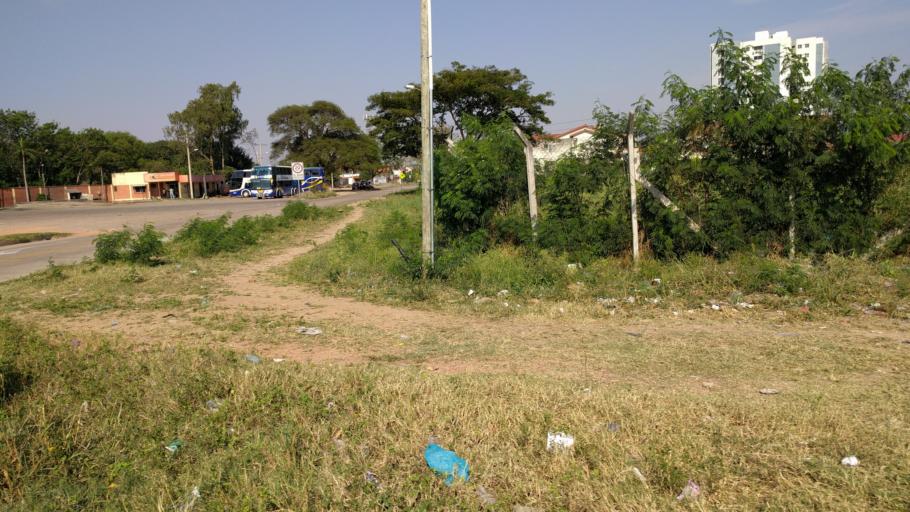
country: BO
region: Santa Cruz
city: Santa Cruz de la Sierra
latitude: -17.8039
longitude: -63.1644
